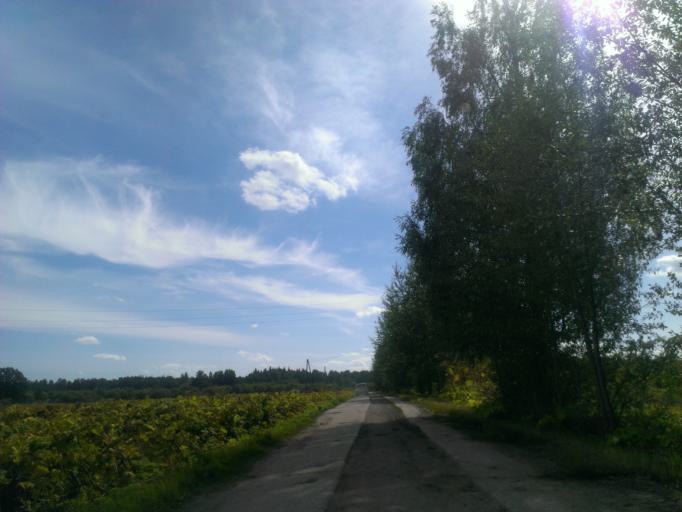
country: LV
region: Ligatne
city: Ligatne
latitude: 57.2267
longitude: 24.9565
